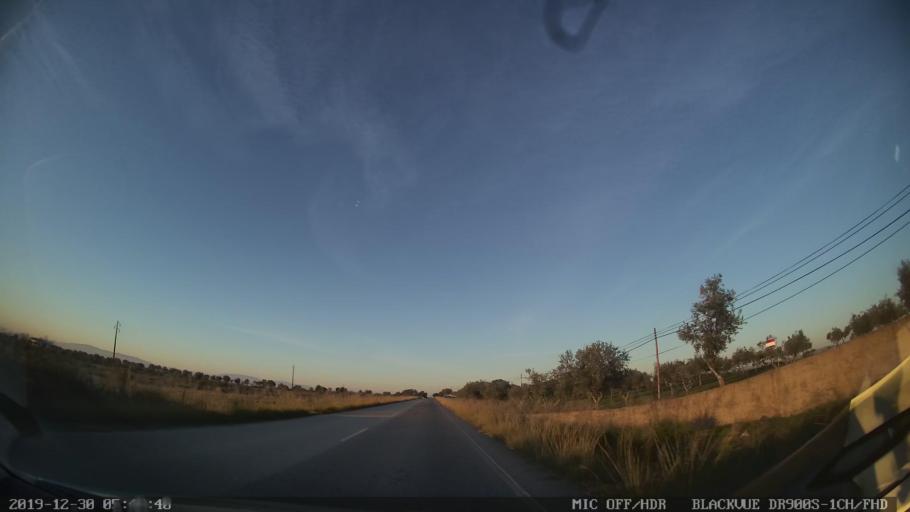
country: PT
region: Castelo Branco
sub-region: Idanha-A-Nova
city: Idanha-a-Nova
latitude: 39.9531
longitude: -7.2407
